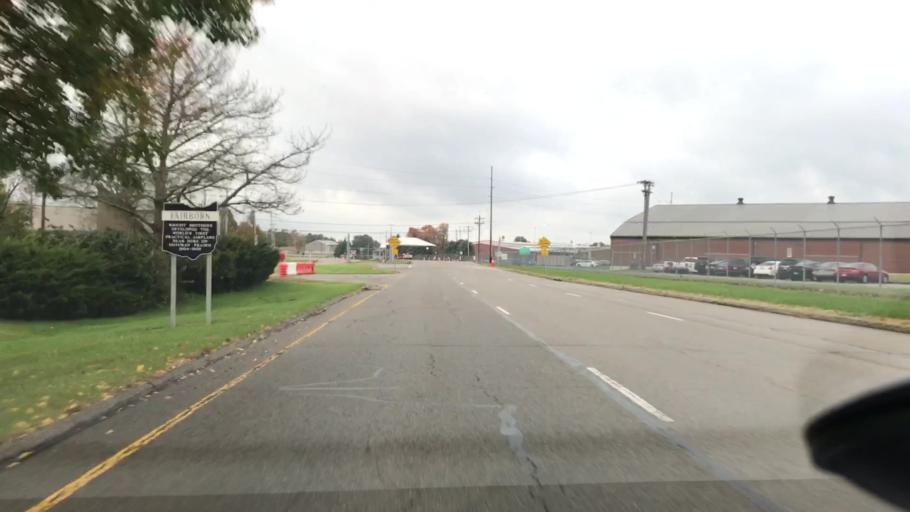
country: US
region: Ohio
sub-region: Greene County
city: Fairborn
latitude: 39.8177
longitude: -84.0296
